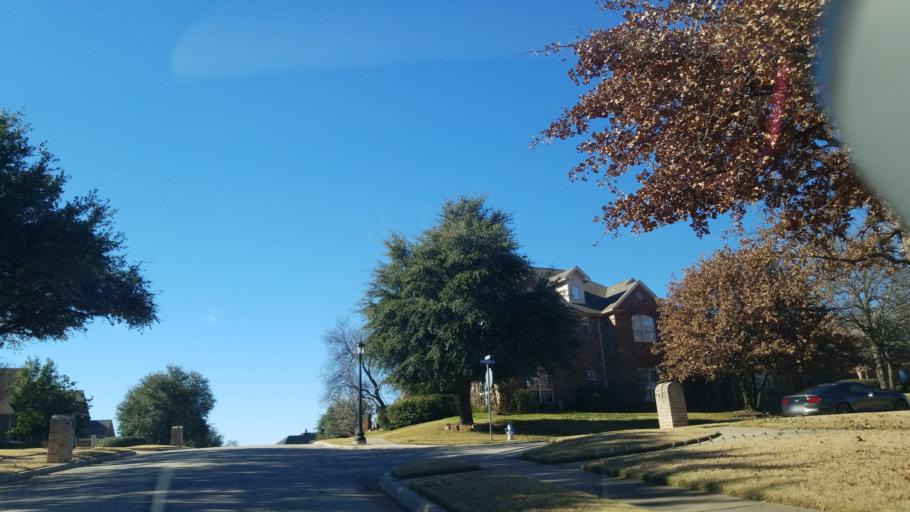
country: US
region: Texas
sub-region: Denton County
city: Corinth
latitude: 33.1523
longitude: -97.0867
